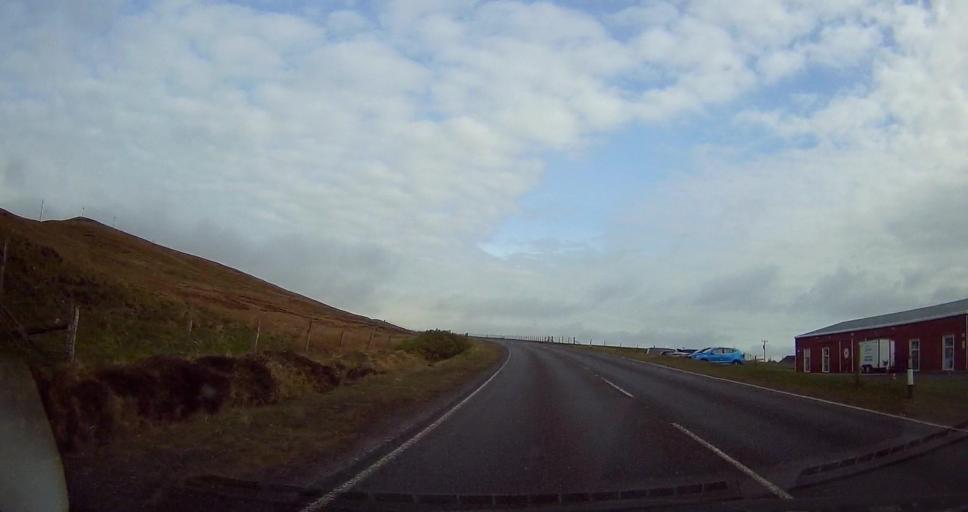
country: GB
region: Scotland
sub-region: Shetland Islands
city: Sandwick
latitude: 60.0620
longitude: -1.2208
